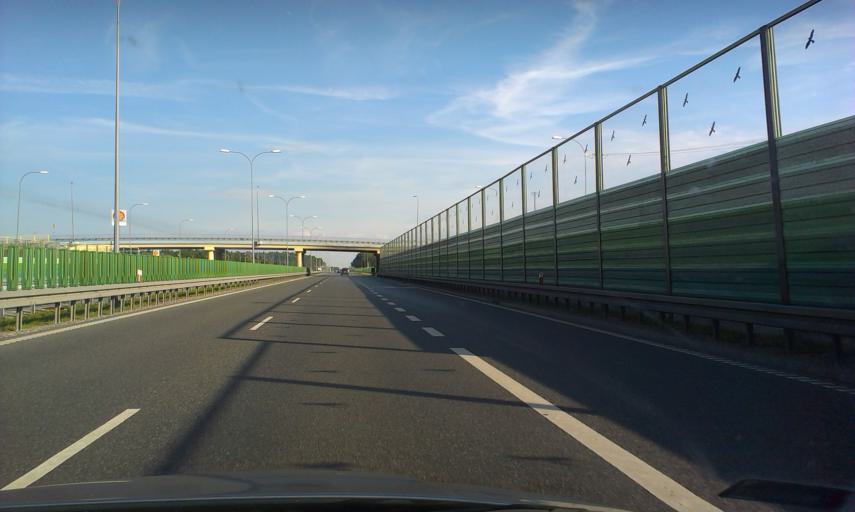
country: PL
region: Kujawsko-Pomorskie
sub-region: Powiat bydgoski
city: Biale Blota
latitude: 53.0894
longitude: 17.9016
